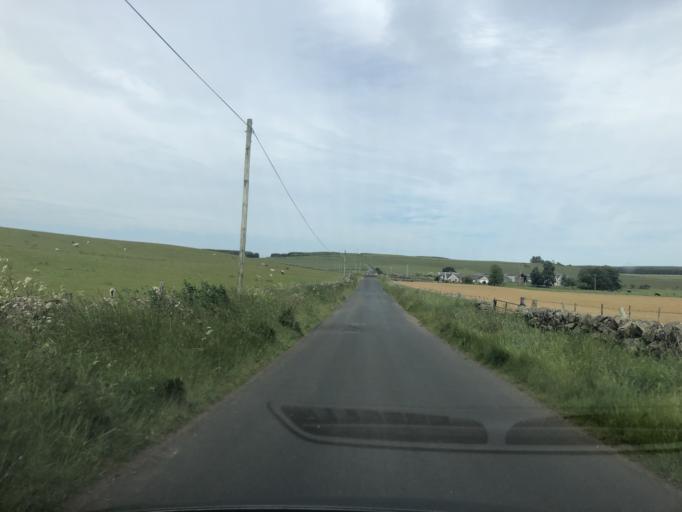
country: GB
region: Scotland
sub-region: The Scottish Borders
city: West Linton
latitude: 55.7614
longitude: -3.3340
